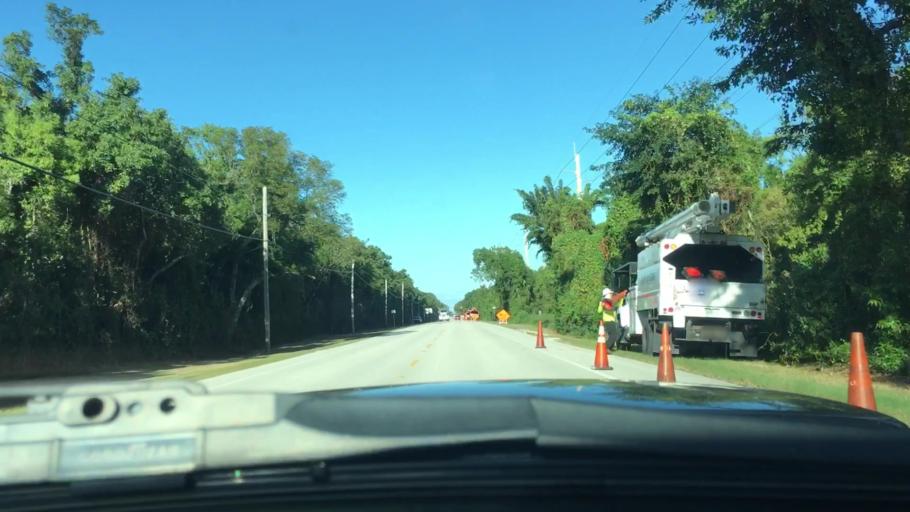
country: US
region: Florida
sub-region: Monroe County
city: North Key Largo
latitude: 25.1857
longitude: -80.3613
